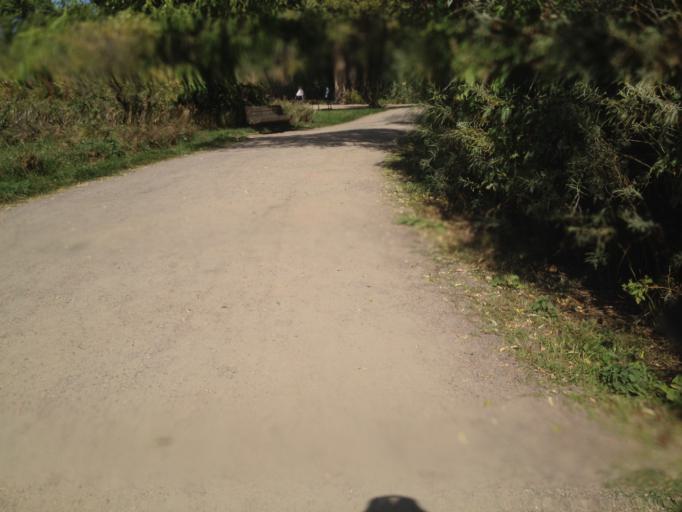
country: US
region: Colorado
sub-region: Boulder County
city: Lafayette
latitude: 39.9964
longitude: -105.1147
